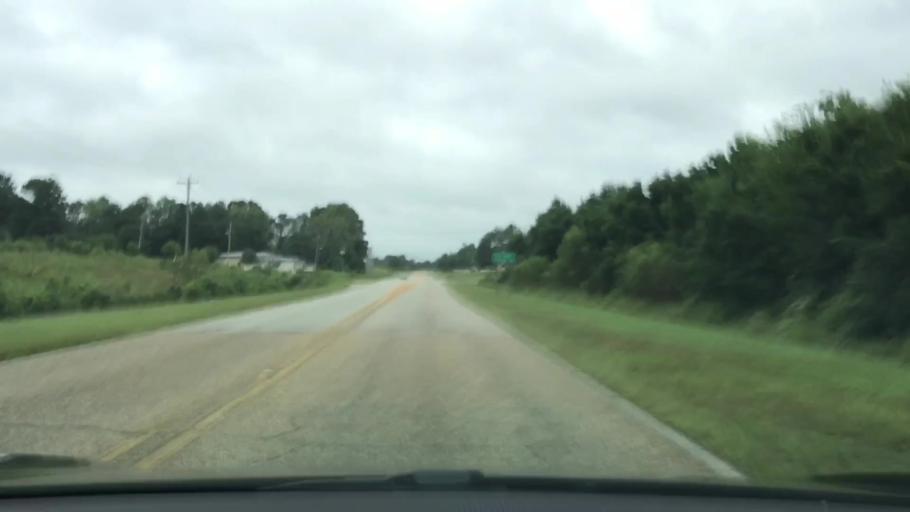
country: US
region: Alabama
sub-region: Coffee County
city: Elba
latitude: 31.4104
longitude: -86.0838
